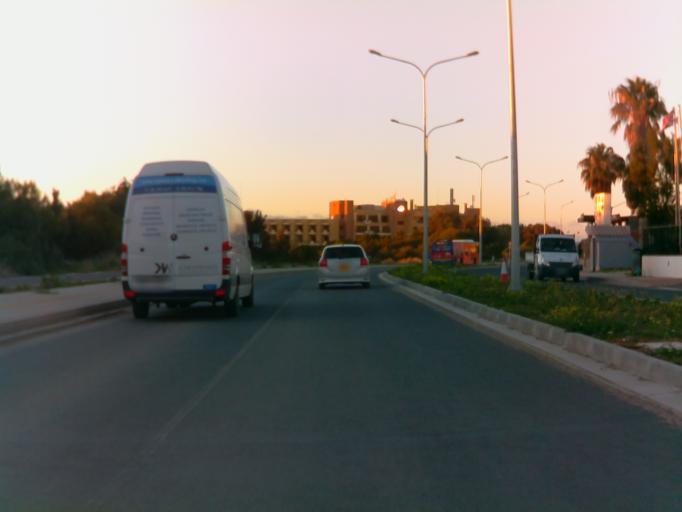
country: CY
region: Pafos
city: Paphos
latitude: 34.7769
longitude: 32.4072
